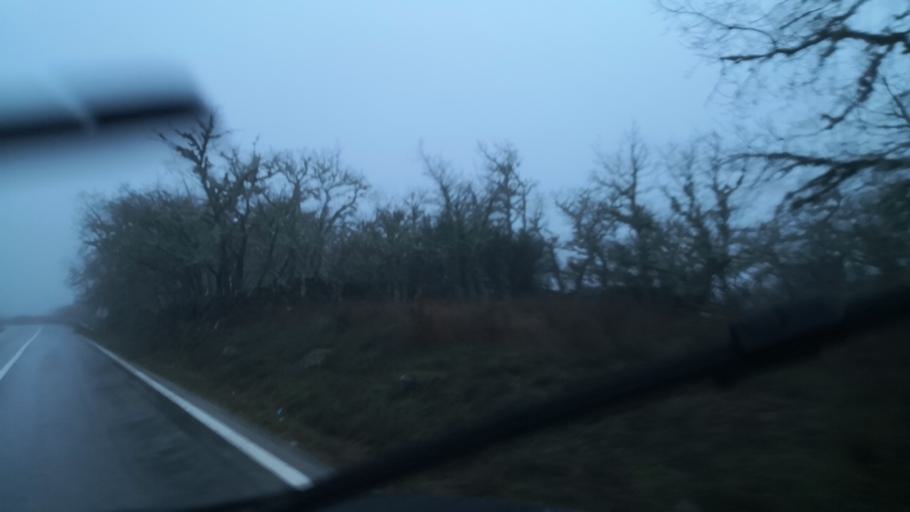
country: PT
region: Vila Real
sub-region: Vila Pouca de Aguiar
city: Vila Pouca de Aguiar
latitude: 41.4963
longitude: -7.6240
